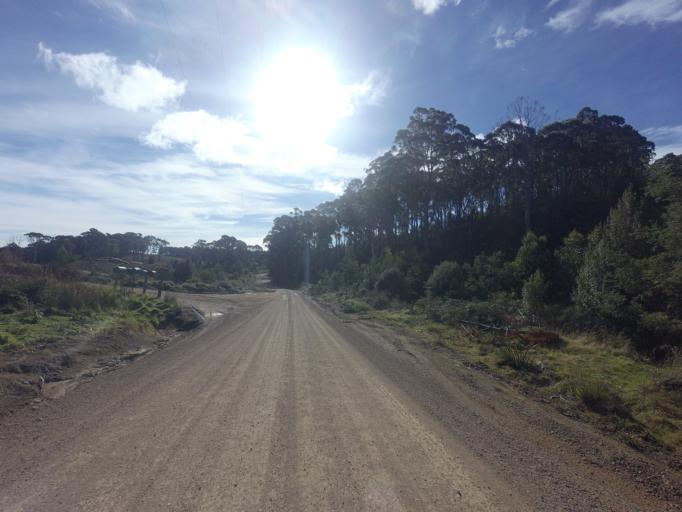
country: AU
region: Tasmania
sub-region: Clarence
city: Sandford
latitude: -43.1736
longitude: 147.7709
